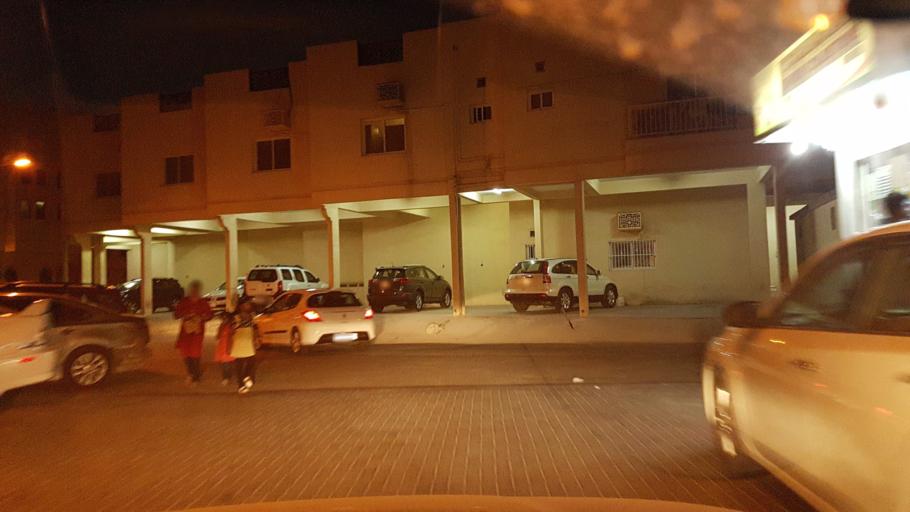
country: BH
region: Manama
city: Manama
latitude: 26.2200
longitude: 50.5750
